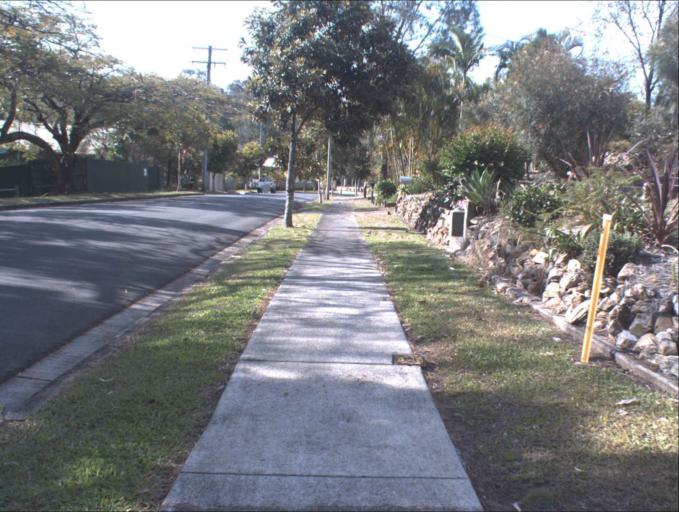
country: AU
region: Queensland
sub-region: Logan
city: Slacks Creek
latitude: -27.6561
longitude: 153.1591
